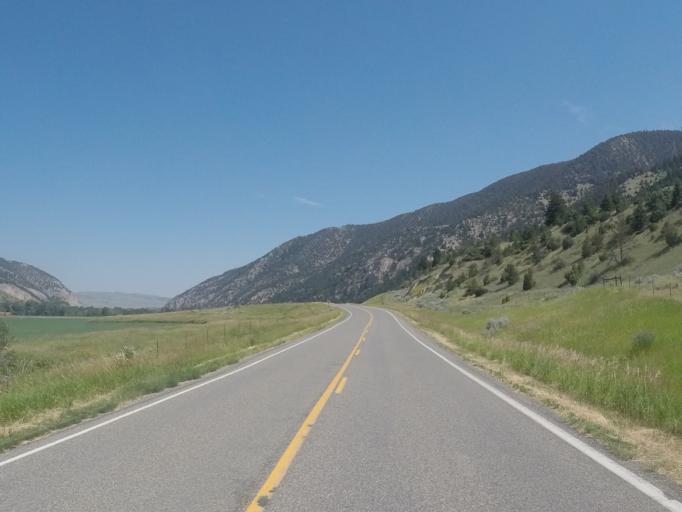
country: US
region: Montana
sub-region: Park County
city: Livingston
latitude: 45.5813
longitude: -110.5626
